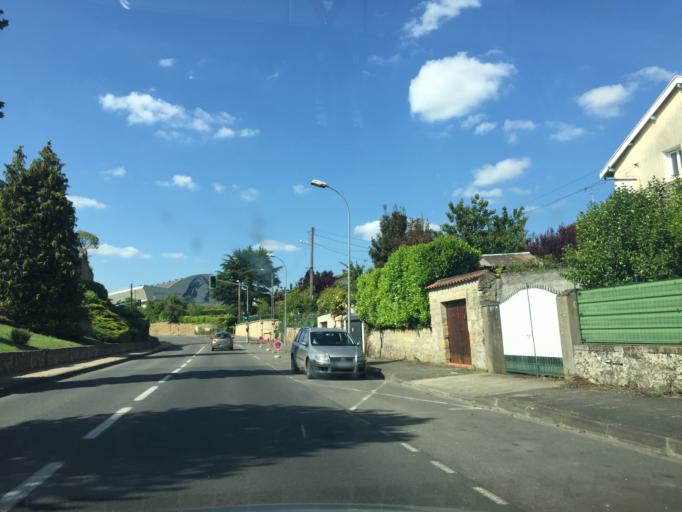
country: FR
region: Aquitaine
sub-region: Departement de la Gironde
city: La Reole
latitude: 44.5821
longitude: -0.0338
